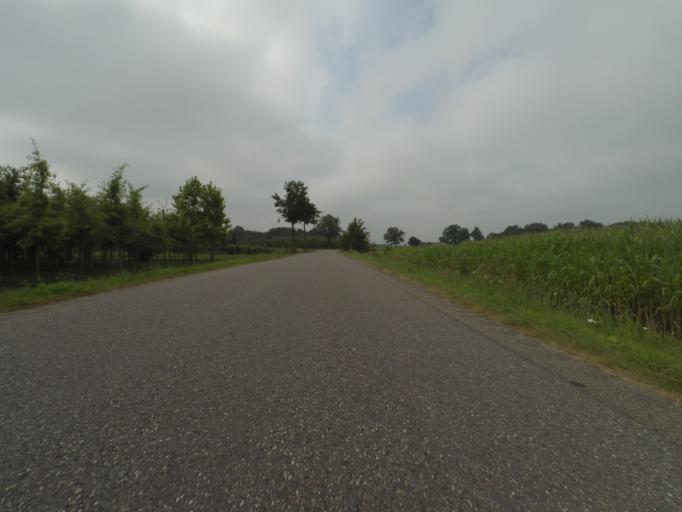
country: NL
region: Gelderland
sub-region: Gemeente Barneveld
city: Kootwijkerbroek
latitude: 52.1308
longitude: 5.6784
